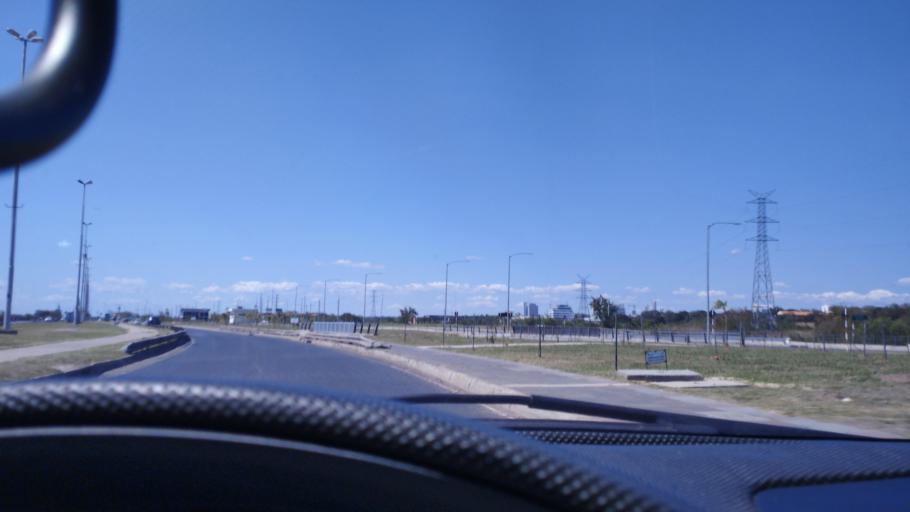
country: PY
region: Asuncion
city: Asuncion
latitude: -25.2765
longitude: -57.6174
